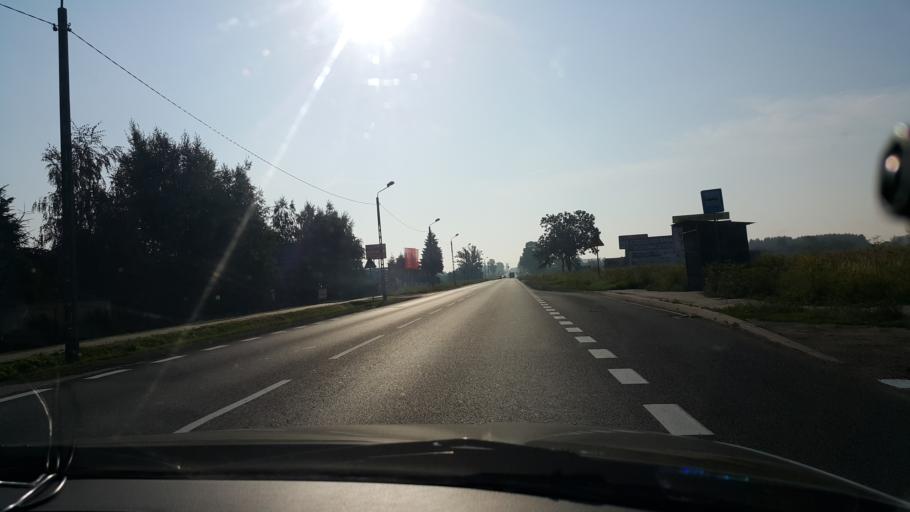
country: PL
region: Masovian Voivodeship
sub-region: Radom
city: Radom
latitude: 51.4145
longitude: 21.2143
